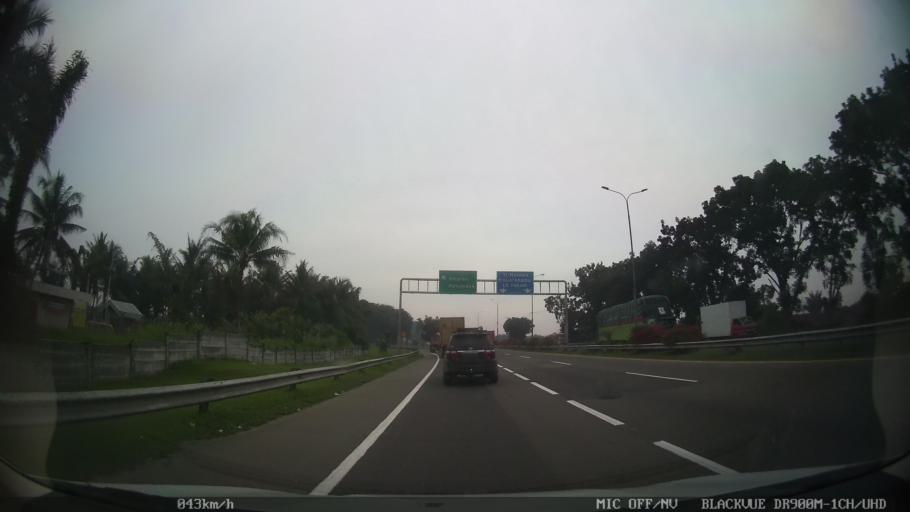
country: ID
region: North Sumatra
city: Deli Tua
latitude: 3.5485
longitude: 98.7251
